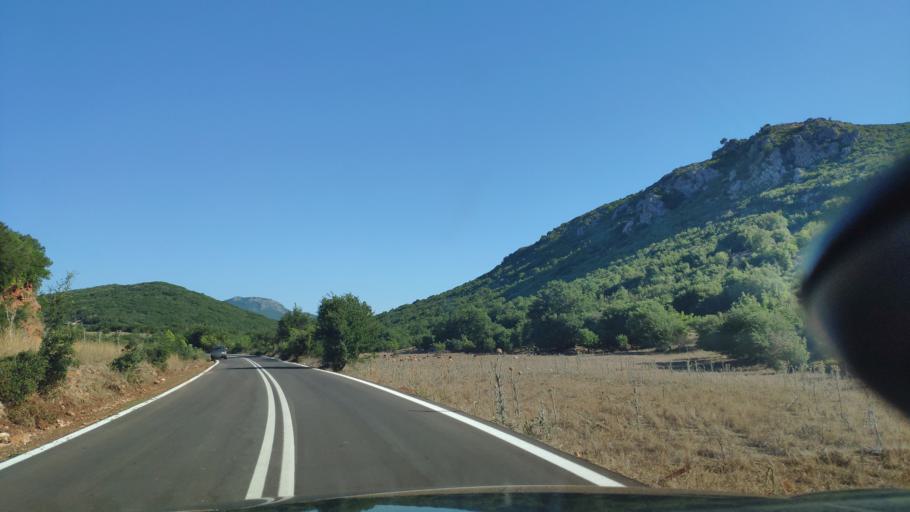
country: GR
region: West Greece
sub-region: Nomos Aitolias kai Akarnanias
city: Fitiai
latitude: 38.6776
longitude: 21.1365
